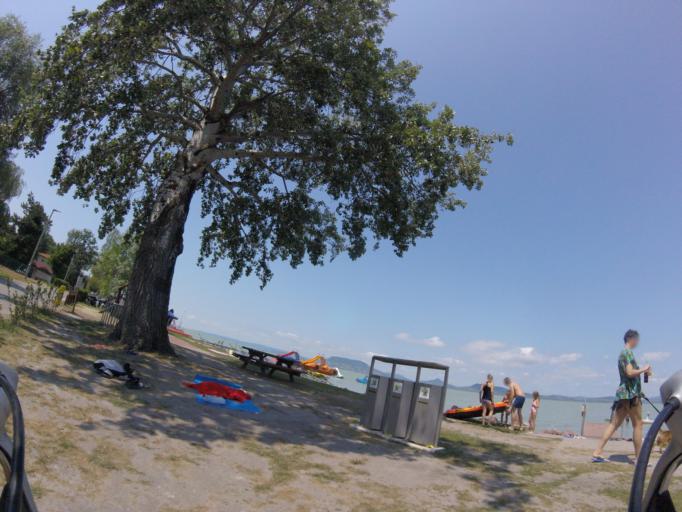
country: HU
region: Somogy
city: Fonyod
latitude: 46.7603
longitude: 17.5919
